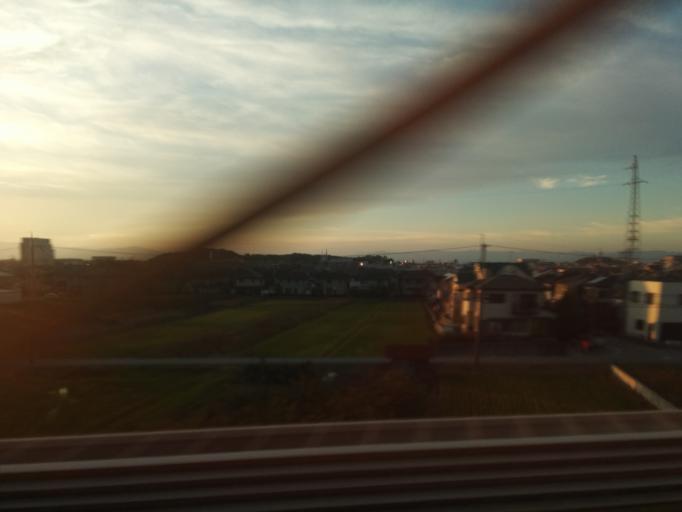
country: JP
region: Shiga Prefecture
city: Hikone
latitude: 35.2507
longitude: 136.2727
